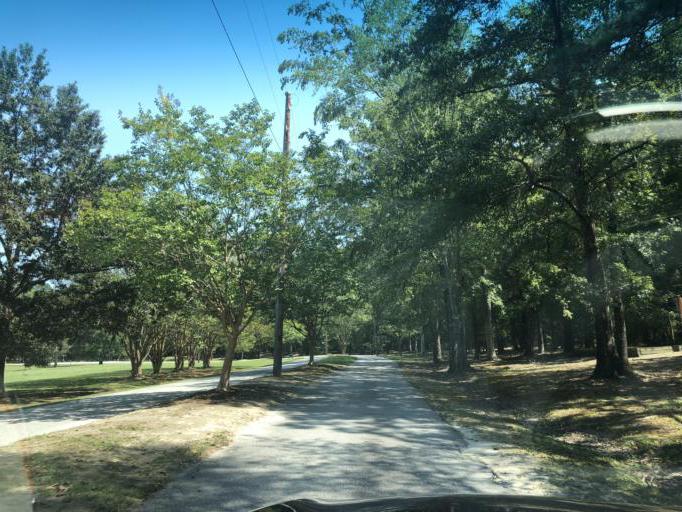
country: US
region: Georgia
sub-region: Muscogee County
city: Columbus
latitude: 32.5092
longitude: -84.9102
